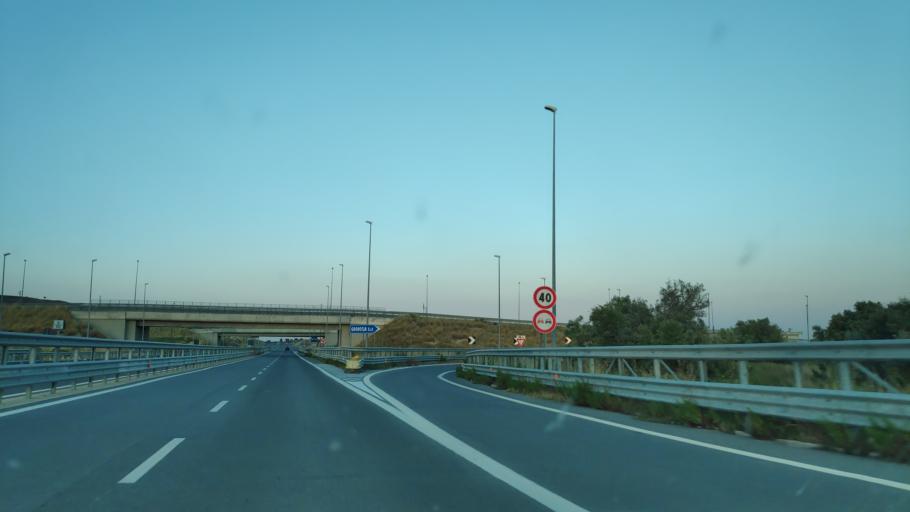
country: IT
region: Calabria
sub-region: Provincia di Reggio Calabria
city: Marina di Gioiosa Ionica
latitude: 38.3103
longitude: 16.3519
